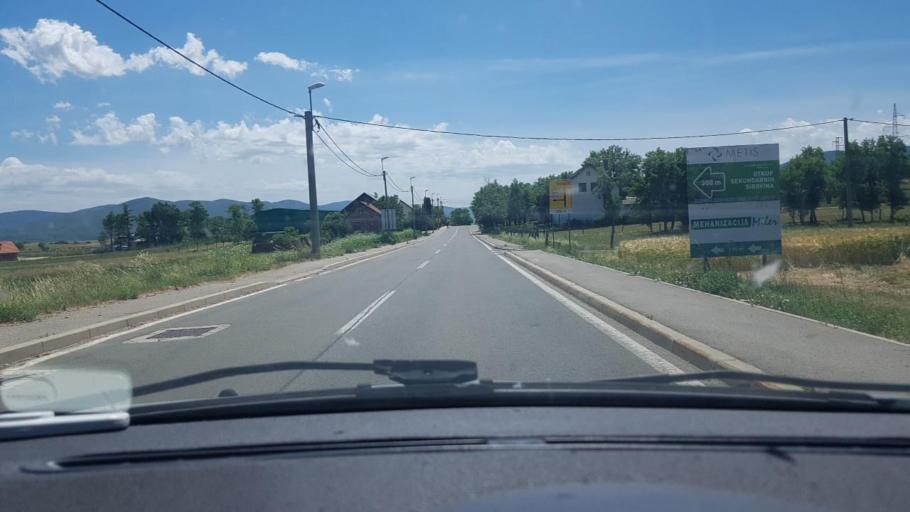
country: HR
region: Licko-Senjska
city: Otocac
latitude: 44.8628
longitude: 15.2610
